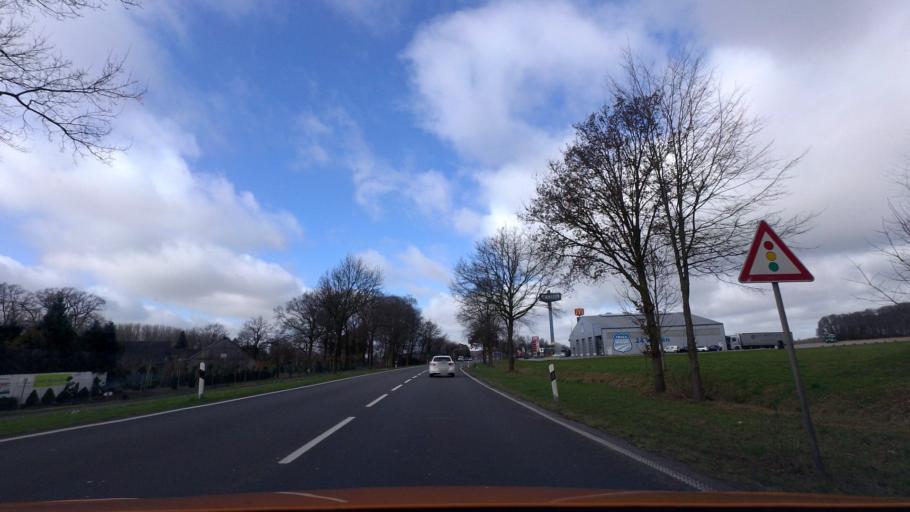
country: DE
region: Lower Saxony
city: Buehren
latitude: 52.8098
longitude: 8.2198
